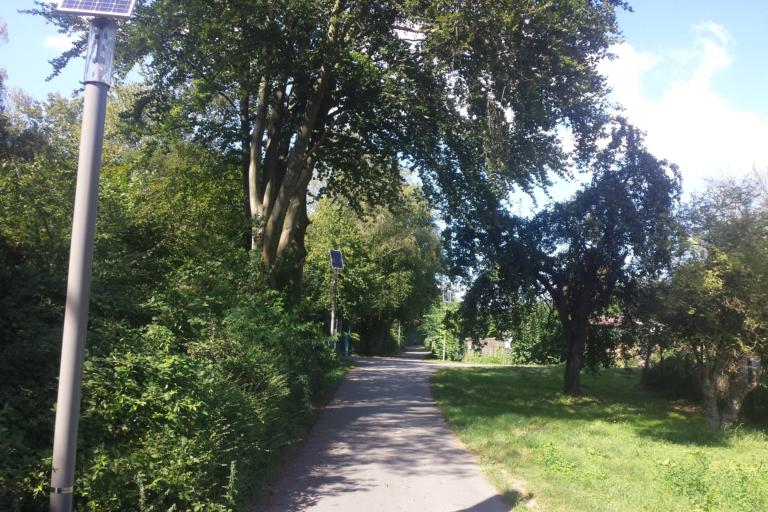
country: DE
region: Baden-Wuerttemberg
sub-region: Karlsruhe Region
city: Hemsbach
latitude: 49.5998
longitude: 8.6542
